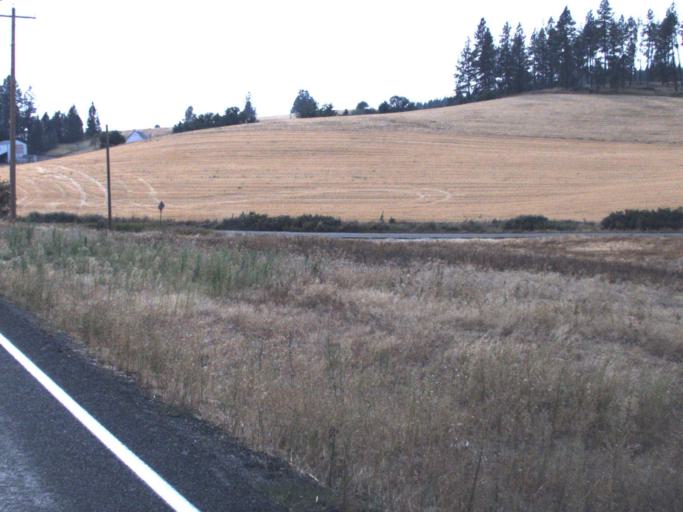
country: US
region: Washington
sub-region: Spokane County
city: Trentwood
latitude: 47.7929
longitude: -117.2492
